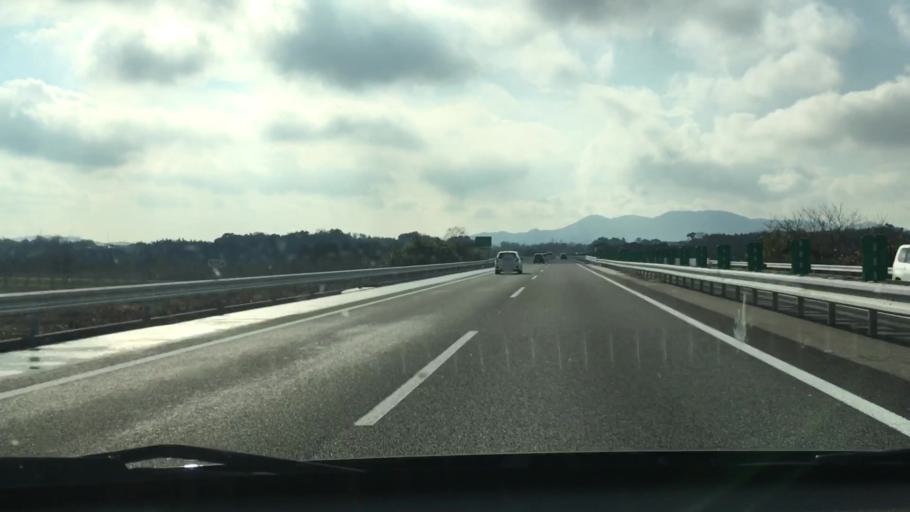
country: JP
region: Kumamoto
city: Uto
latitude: 32.7138
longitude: 130.7644
